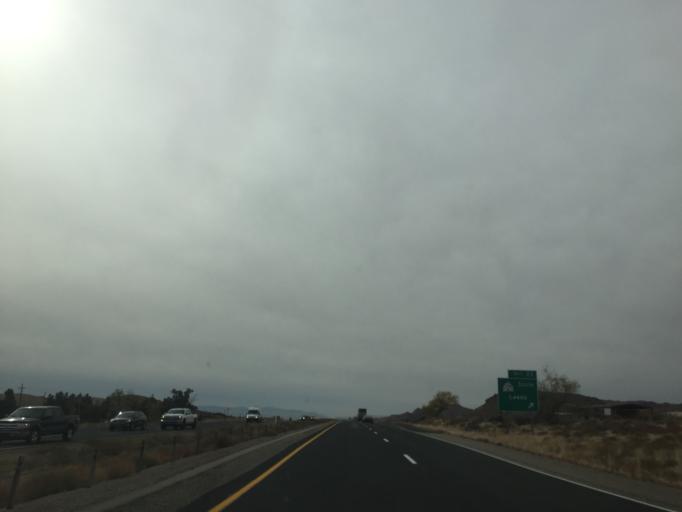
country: US
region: Utah
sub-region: Washington County
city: Toquerville
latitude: 37.2478
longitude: -113.3477
